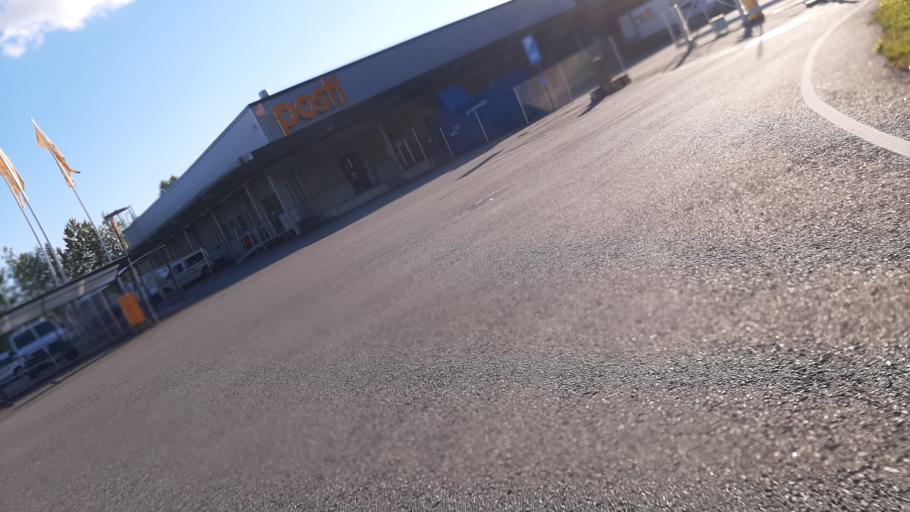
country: FI
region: North Karelia
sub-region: Joensuu
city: Joensuu
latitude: 62.6235
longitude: 29.7704
